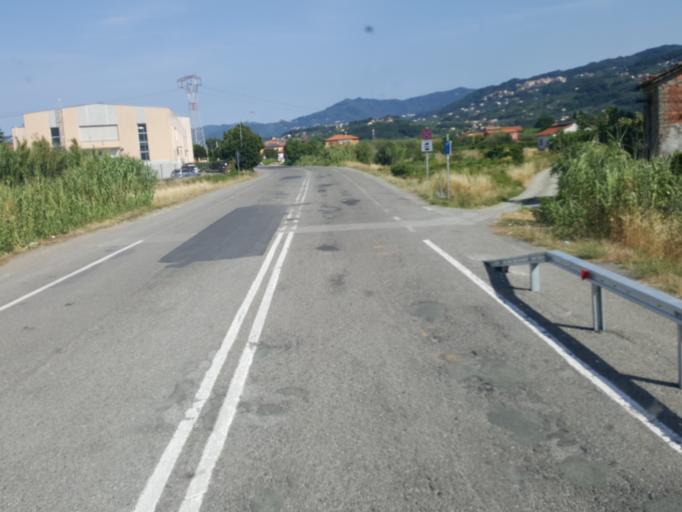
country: IT
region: Liguria
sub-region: Provincia di La Spezia
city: Santo Stefano di Magra
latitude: 44.1554
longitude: 9.9114
